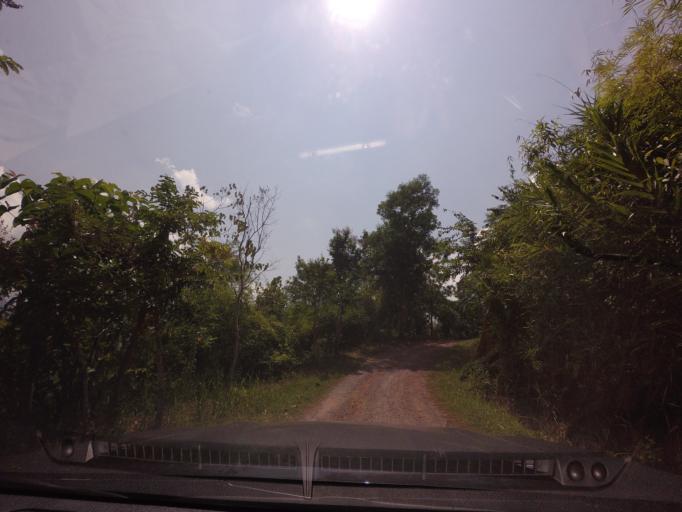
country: TH
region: Nan
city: Bo Kluea
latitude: 19.0153
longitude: 101.2056
